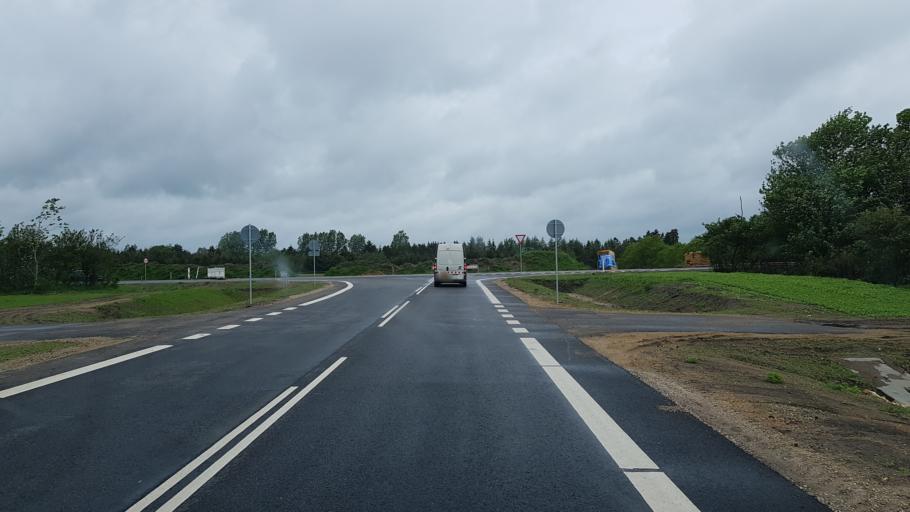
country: DK
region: Central Jutland
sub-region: Skive Kommune
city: Skive
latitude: 56.4028
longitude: 8.9732
